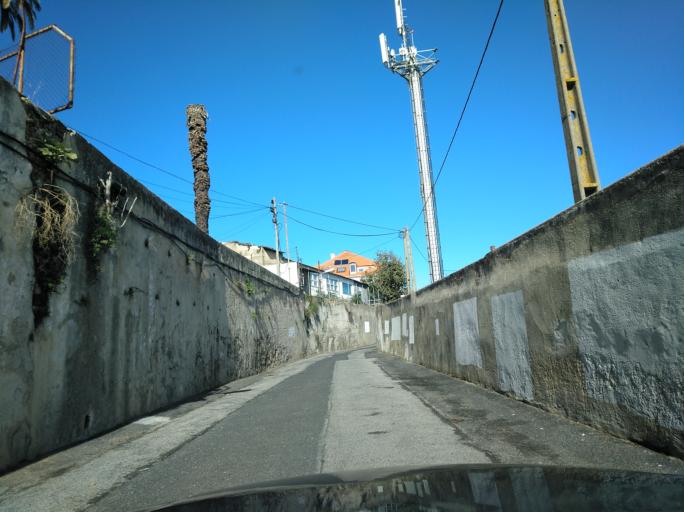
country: PT
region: Lisbon
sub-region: Lisbon
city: Lisbon
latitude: 38.7316
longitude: -9.1099
